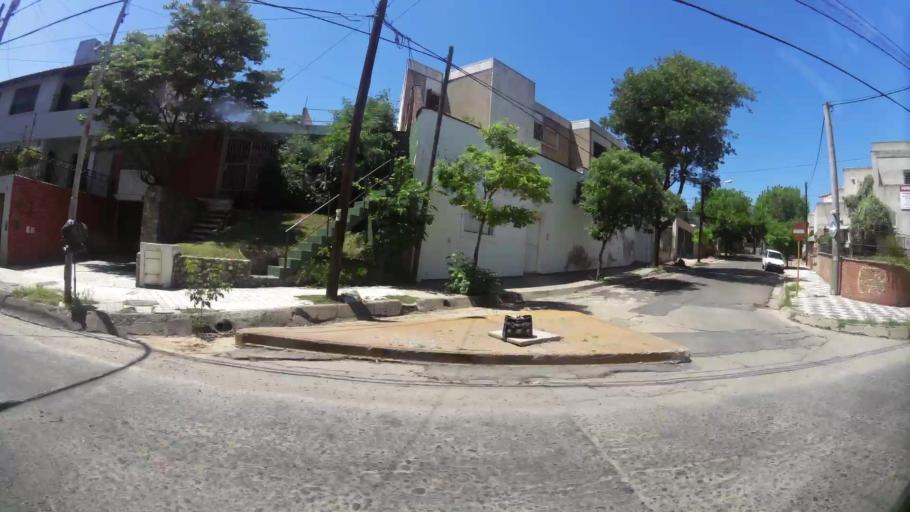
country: AR
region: Cordoba
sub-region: Departamento de Capital
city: Cordoba
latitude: -31.4147
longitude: -64.2032
